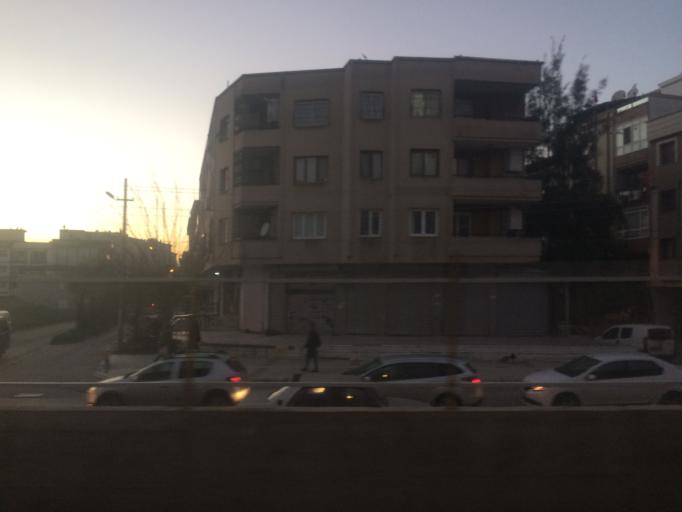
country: TR
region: Izmir
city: Karabaglar
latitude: 38.3820
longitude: 27.1469
